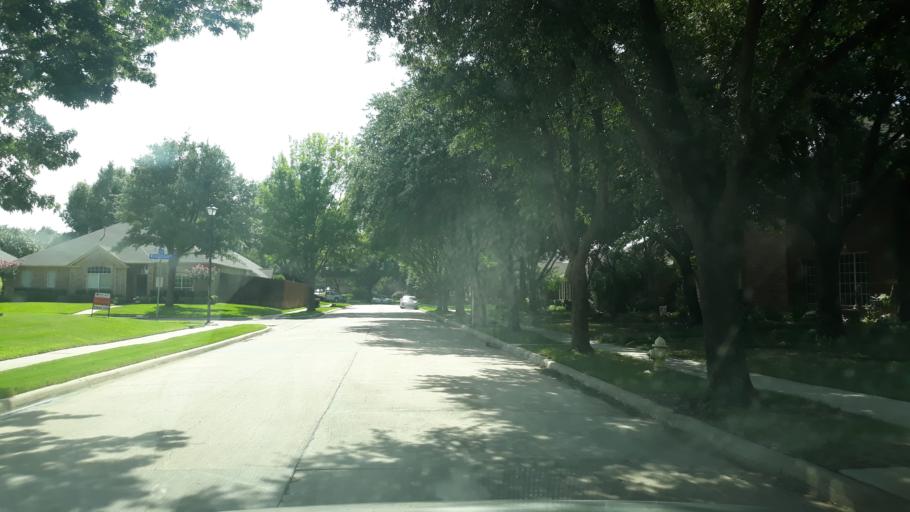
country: US
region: Texas
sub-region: Dallas County
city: Coppell
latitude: 32.9673
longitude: -97.0046
